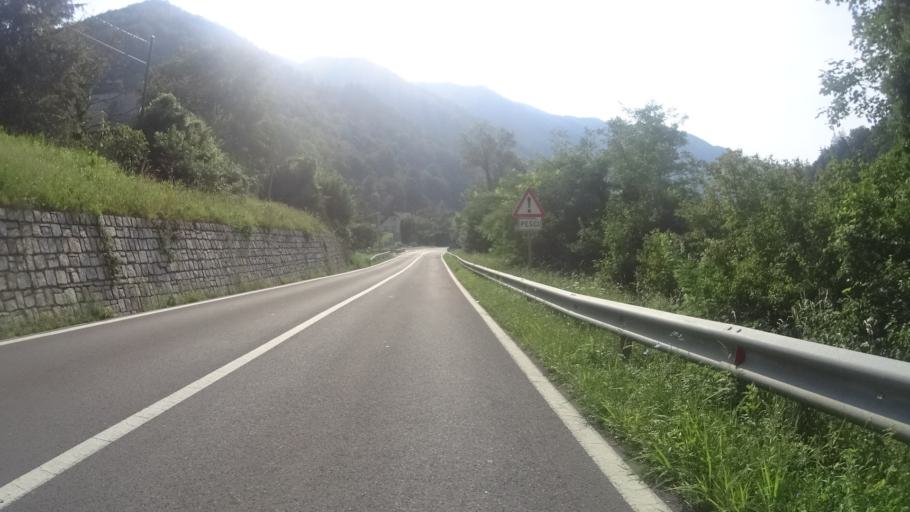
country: SI
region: Selnica ob Dravi
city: Selnica ob Dravi
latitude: 46.5832
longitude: 15.4437
